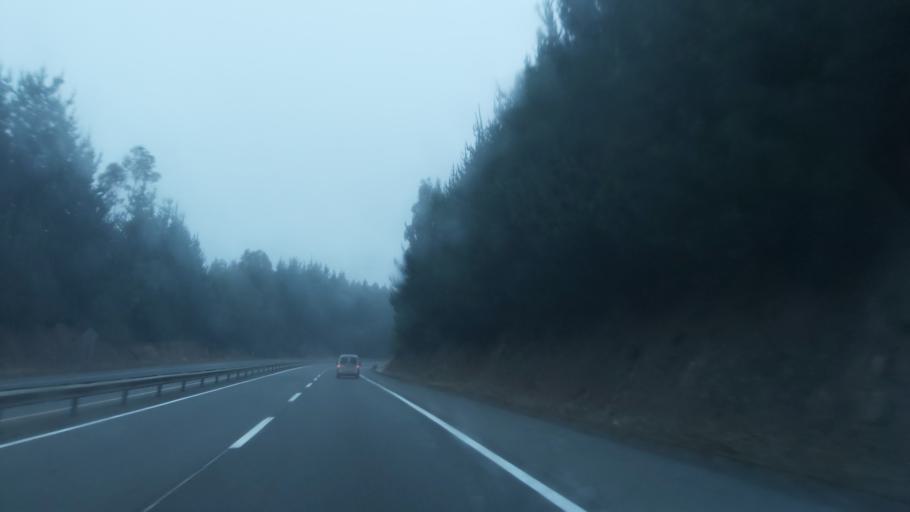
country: CL
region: Biobio
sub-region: Provincia de Concepcion
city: Penco
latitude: -36.7397
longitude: -72.9021
